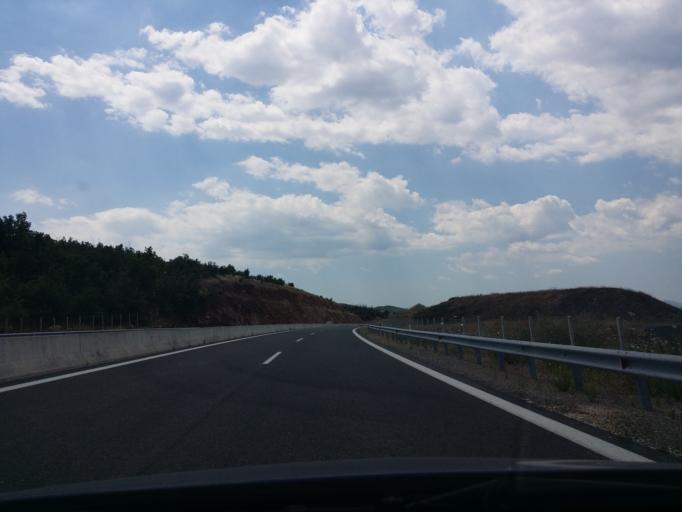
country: GR
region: Peloponnese
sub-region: Nomos Arkadias
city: Megalopoli
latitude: 37.3067
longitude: 22.1860
